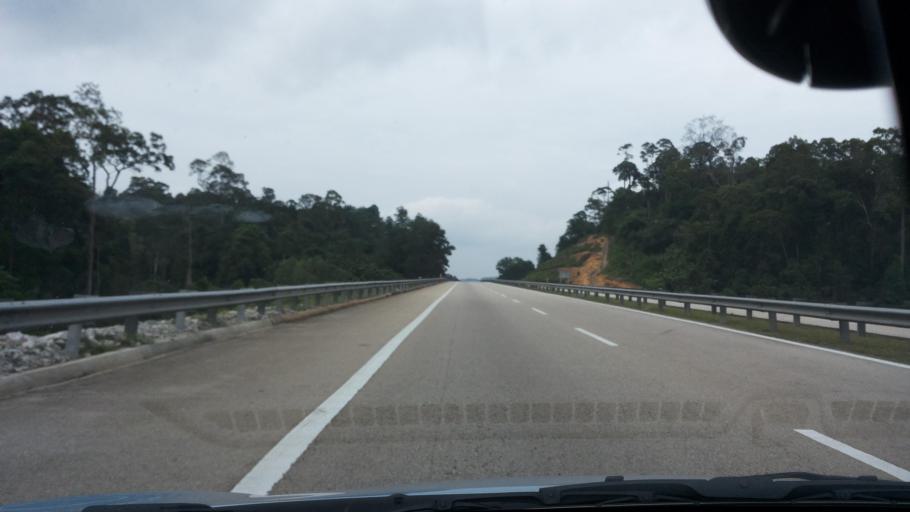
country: MY
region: Pahang
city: Kuantan
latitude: 3.7698
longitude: 103.1461
